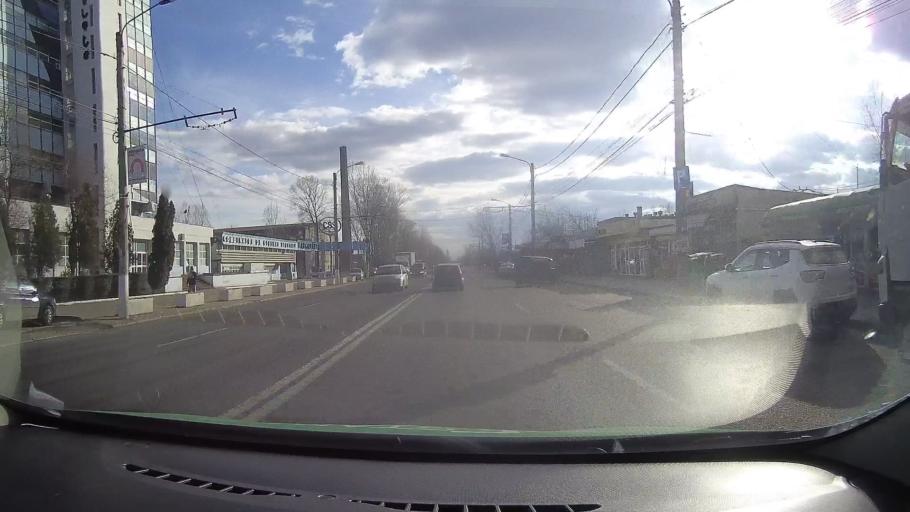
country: RO
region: Dambovita
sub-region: Comuna Lucieni
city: Lucieni
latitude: 44.8502
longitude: 25.4368
